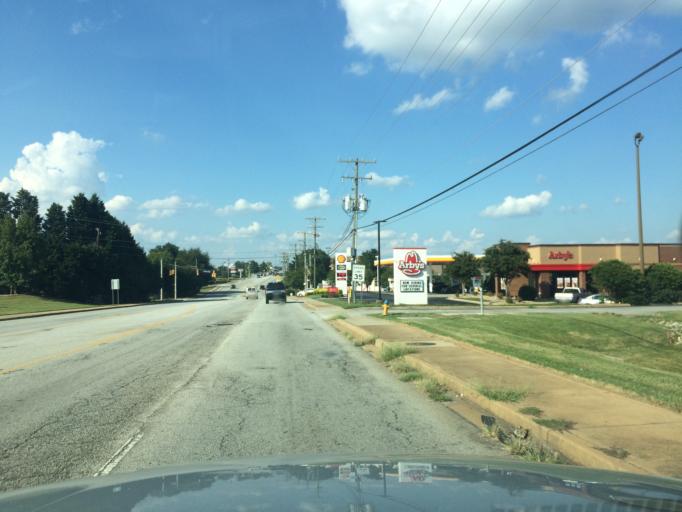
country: US
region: South Carolina
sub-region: Greenville County
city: Simpsonville
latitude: 34.7127
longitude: -82.2562
